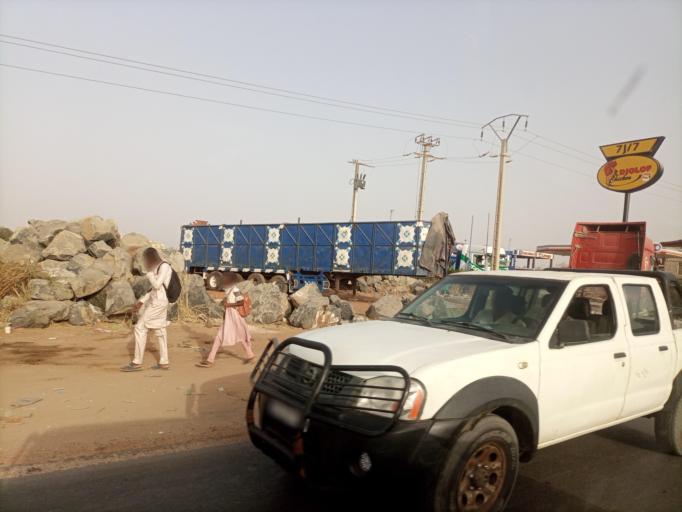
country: SN
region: Thies
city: Nguekhokh
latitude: 14.4595
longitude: -16.9854
